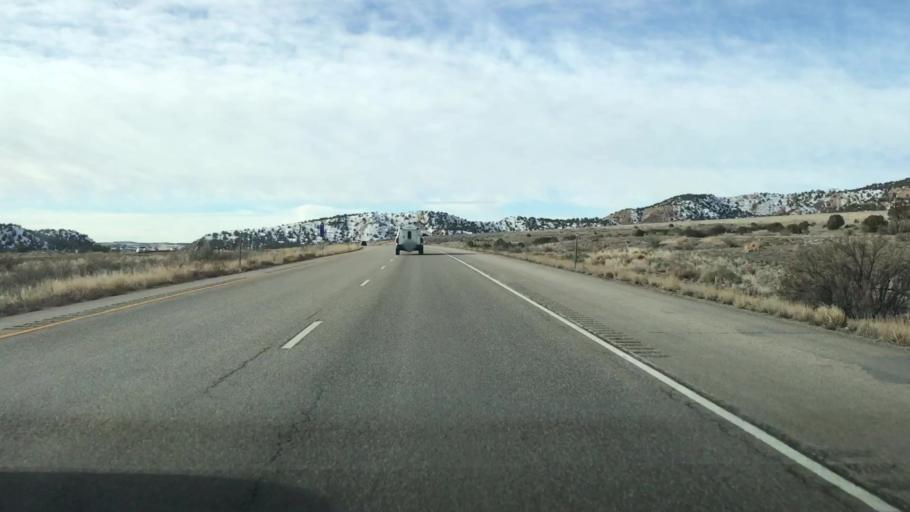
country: US
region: Colorado
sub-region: Garfield County
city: Parachute
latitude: 39.3854
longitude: -108.1475
